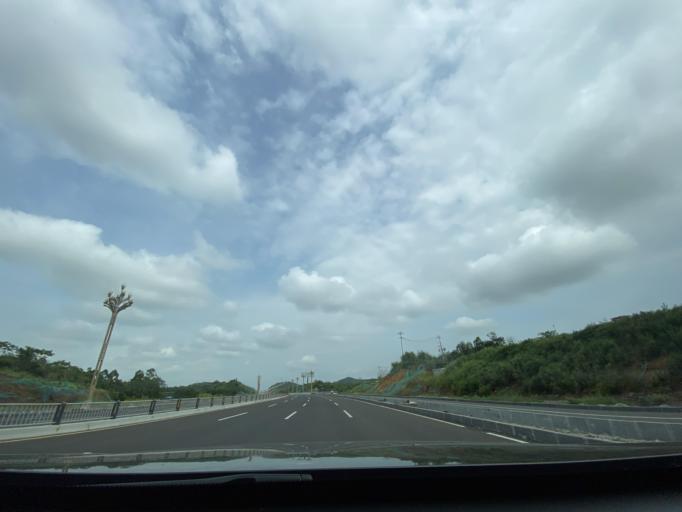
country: CN
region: Sichuan
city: Jiancheng
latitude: 30.3875
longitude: 104.6159
